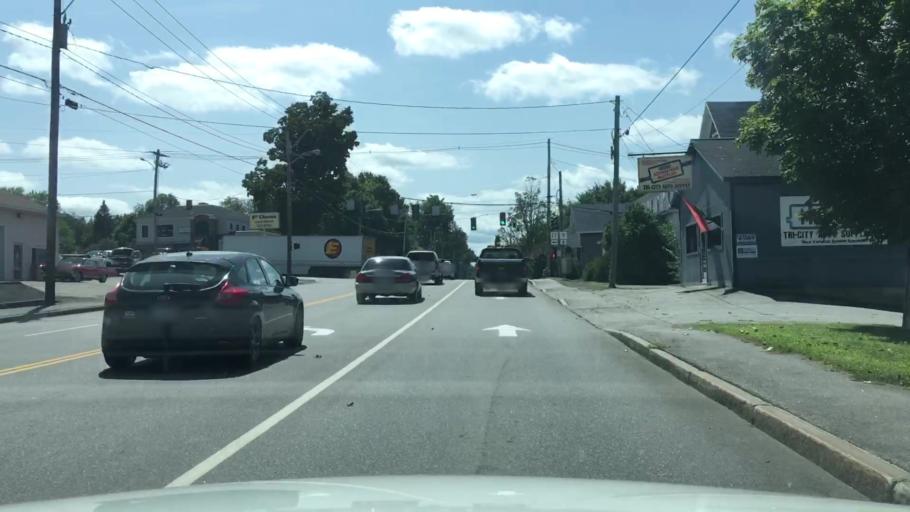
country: US
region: Maine
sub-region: Kennebec County
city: Augusta
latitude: 44.3105
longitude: -69.7647
